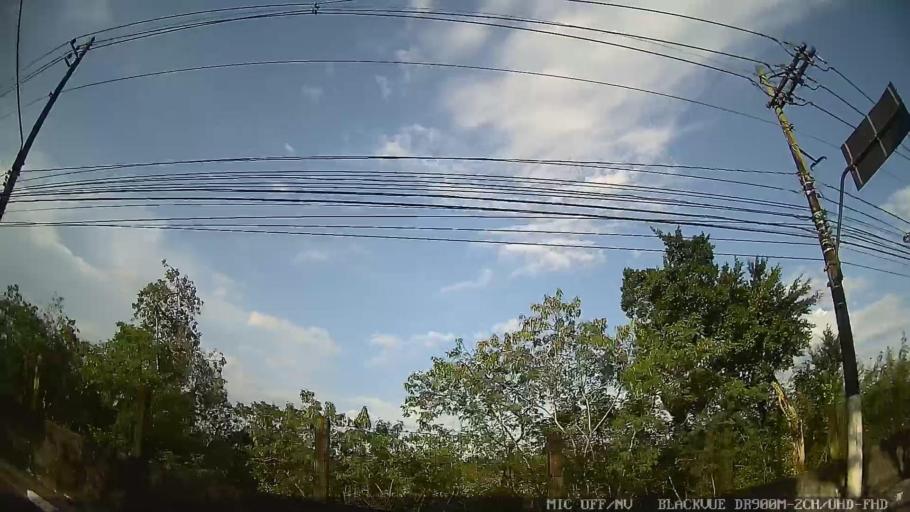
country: BR
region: Sao Paulo
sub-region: Cubatao
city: Cubatao
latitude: -23.9032
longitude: -46.4231
